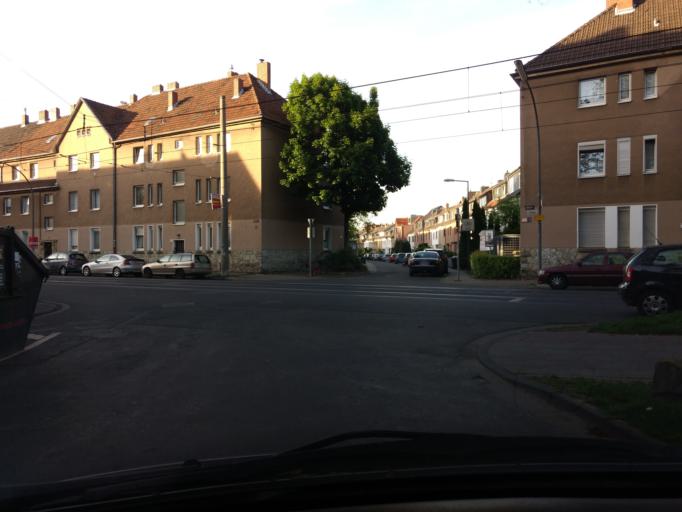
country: DE
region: North Rhine-Westphalia
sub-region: Regierungsbezirk Koln
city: Bilderstoeckchen
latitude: 50.9615
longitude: 6.9156
